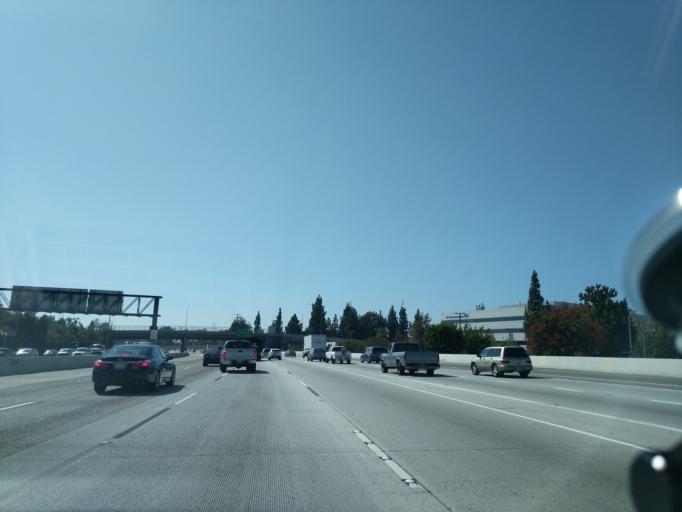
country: US
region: California
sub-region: Orange County
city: Orange
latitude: 33.7791
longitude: -117.8940
